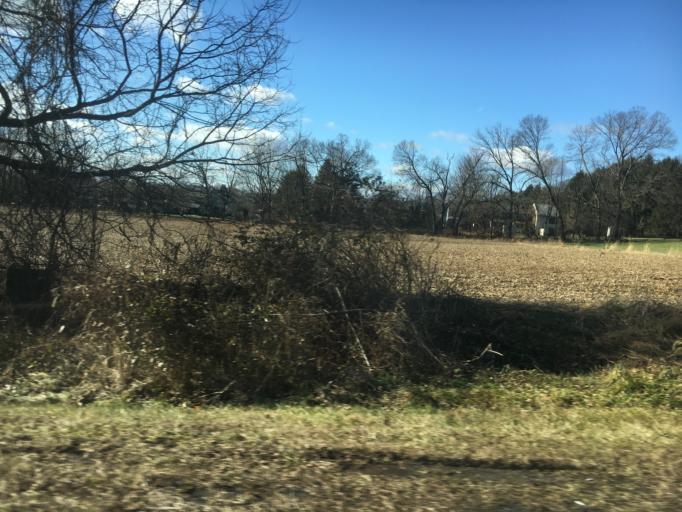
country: US
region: Pennsylvania
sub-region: Lehigh County
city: Dorneyville
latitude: 40.6175
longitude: -75.5351
